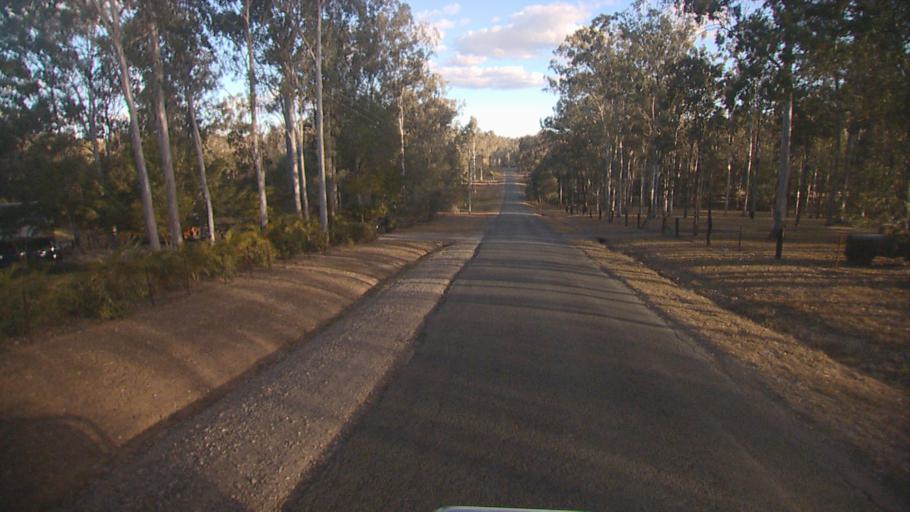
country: AU
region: Queensland
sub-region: Logan
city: Cedar Vale
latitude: -27.8524
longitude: 153.0892
